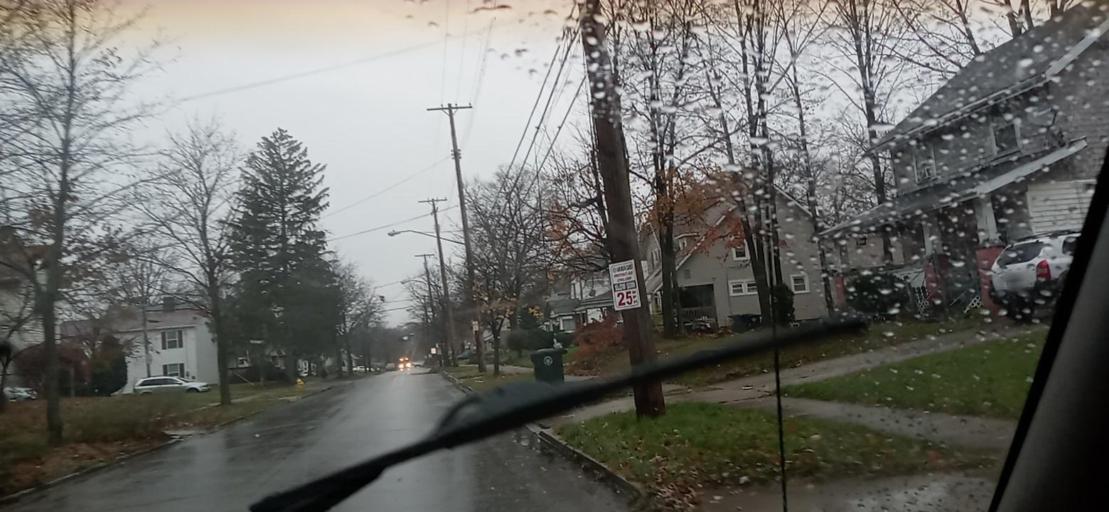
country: US
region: Ohio
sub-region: Summit County
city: Akron
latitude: 41.0868
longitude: -81.5476
